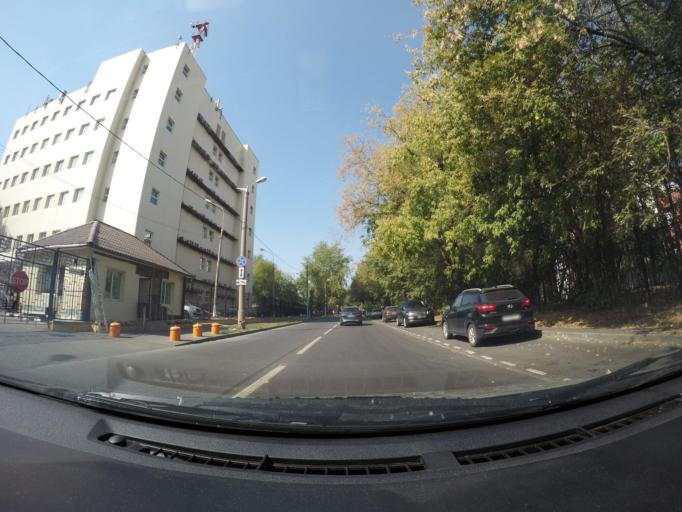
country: RU
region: Moscow
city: Sokol'niki
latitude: 55.7873
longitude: 37.6718
